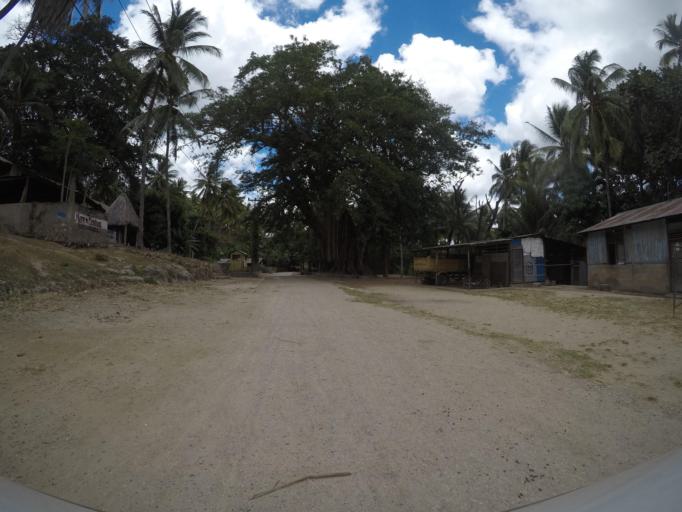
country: TL
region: Lautem
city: Lospalos
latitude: -8.3799
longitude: 126.9229
